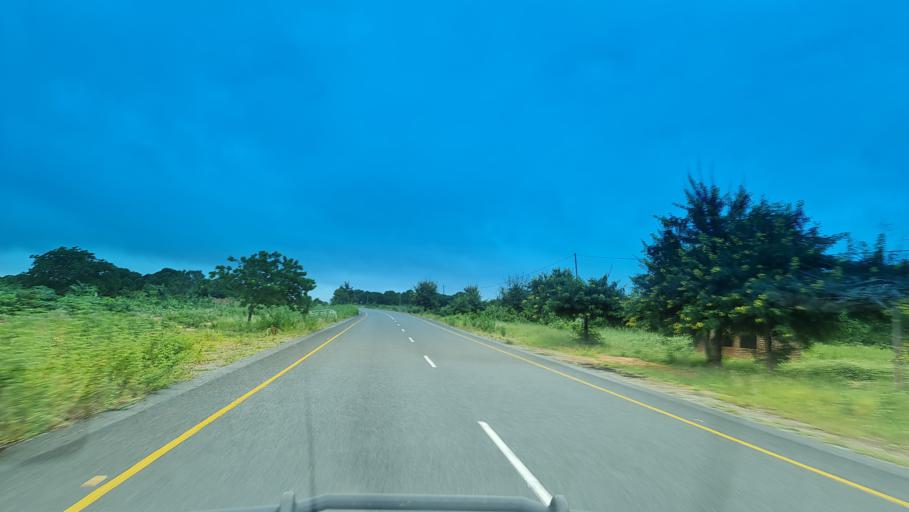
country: MZ
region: Nampula
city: Nampula
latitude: -15.6032
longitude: 39.3274
